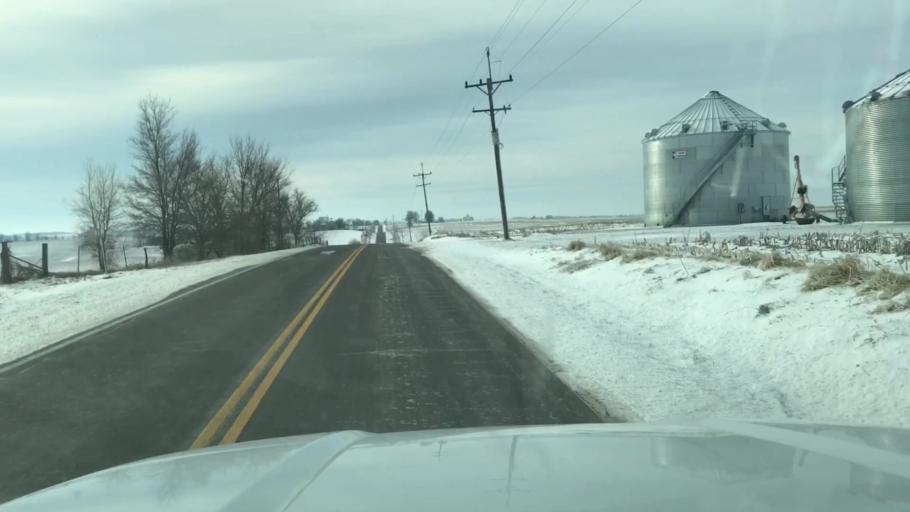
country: US
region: Missouri
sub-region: Holt County
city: Oregon
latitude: 40.0709
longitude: -95.1356
